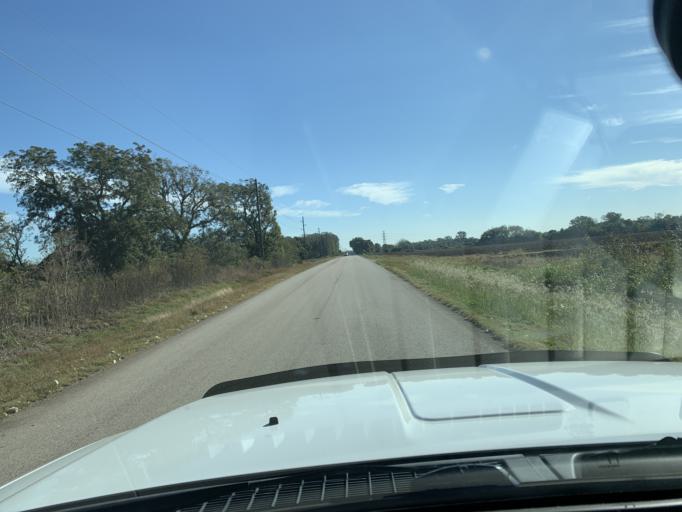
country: US
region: Texas
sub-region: Fort Bend County
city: Rosenberg
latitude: 29.6213
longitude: -95.8257
